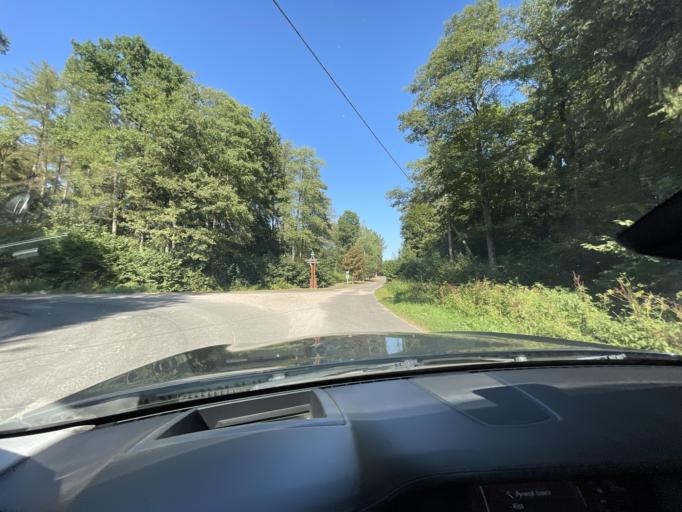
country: BY
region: Grodnenskaya
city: Hrodna
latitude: 53.7515
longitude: 23.9784
